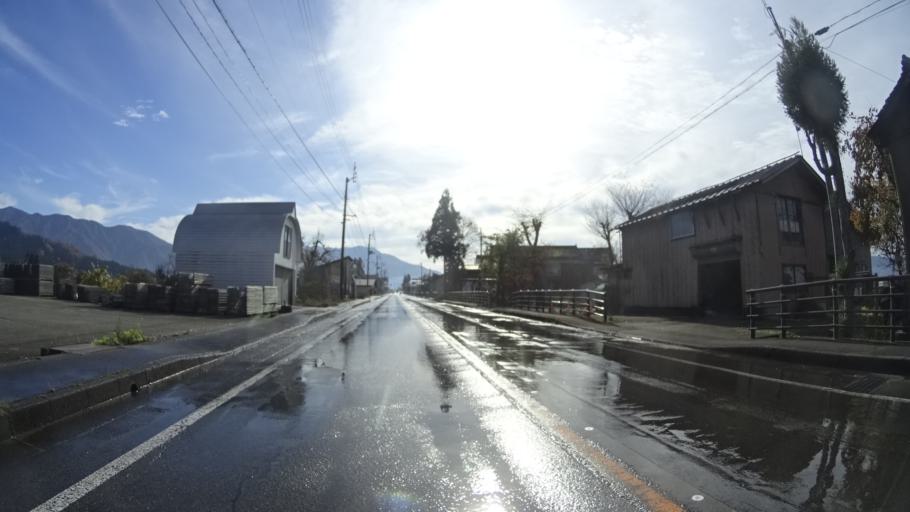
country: JP
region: Niigata
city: Muikamachi
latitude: 37.1109
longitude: 138.9213
